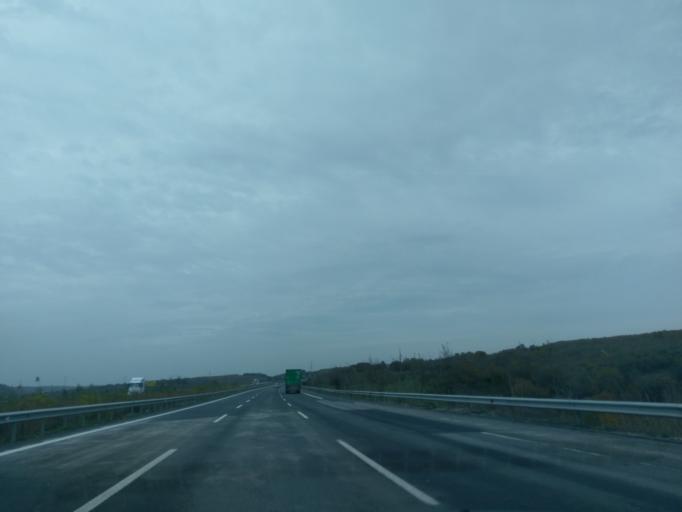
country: TR
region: Istanbul
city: Canta
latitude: 41.1736
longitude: 28.1180
